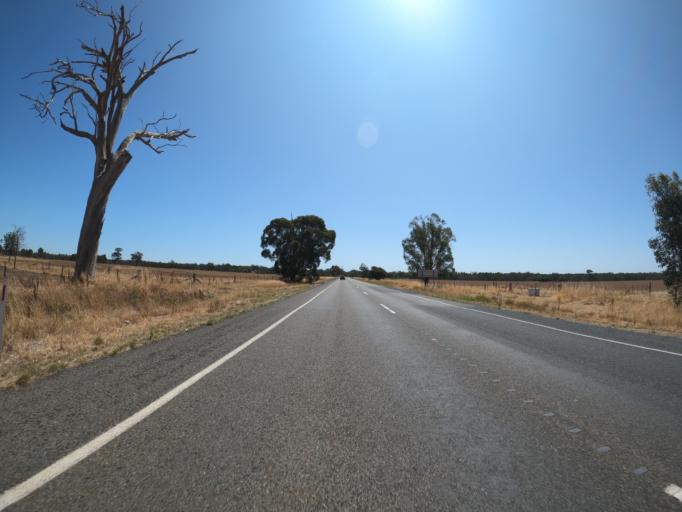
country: AU
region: New South Wales
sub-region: Corowa Shire
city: Corowa
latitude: -36.0708
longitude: 146.2132
